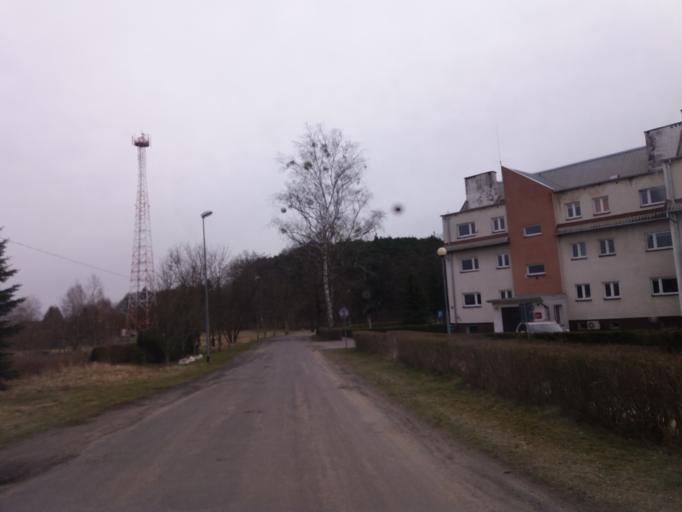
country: PL
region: West Pomeranian Voivodeship
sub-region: Powiat choszczenski
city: Drawno
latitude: 53.2137
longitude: 15.7414
